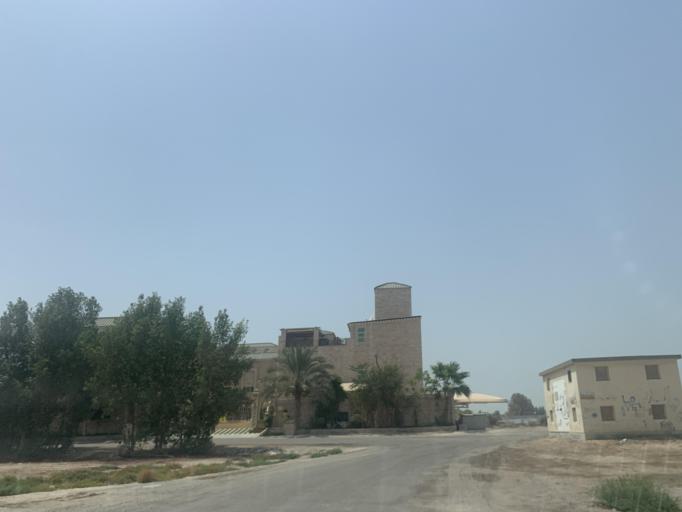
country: BH
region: Manama
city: Jidd Hafs
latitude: 26.2008
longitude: 50.5044
